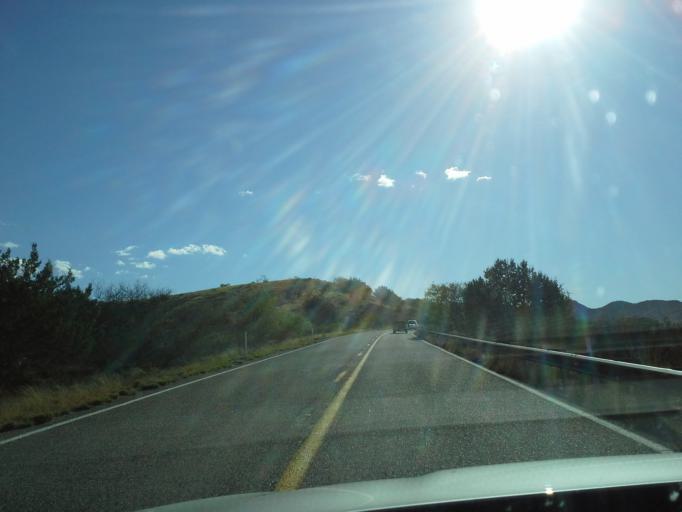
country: US
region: Arizona
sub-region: Pima County
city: Corona de Tucson
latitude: 31.8318
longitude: -110.7065
